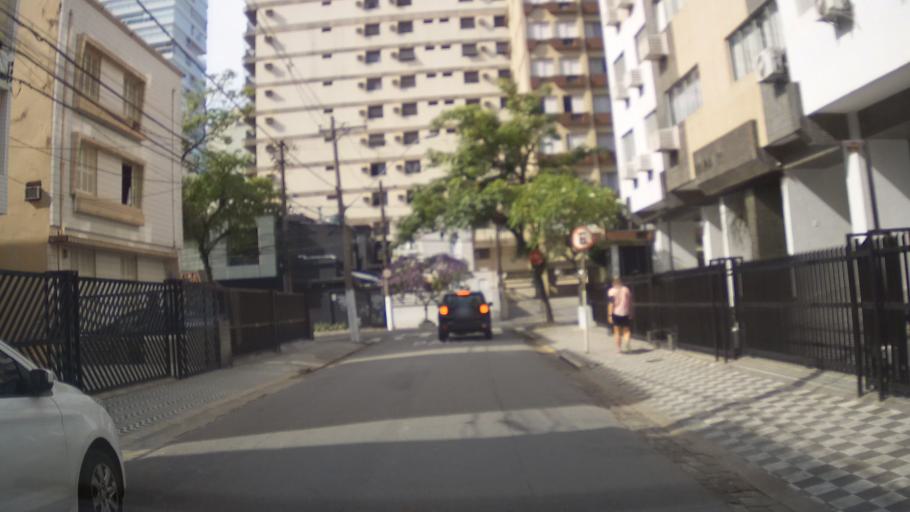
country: BR
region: Sao Paulo
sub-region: Santos
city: Santos
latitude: -23.9658
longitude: -46.3310
